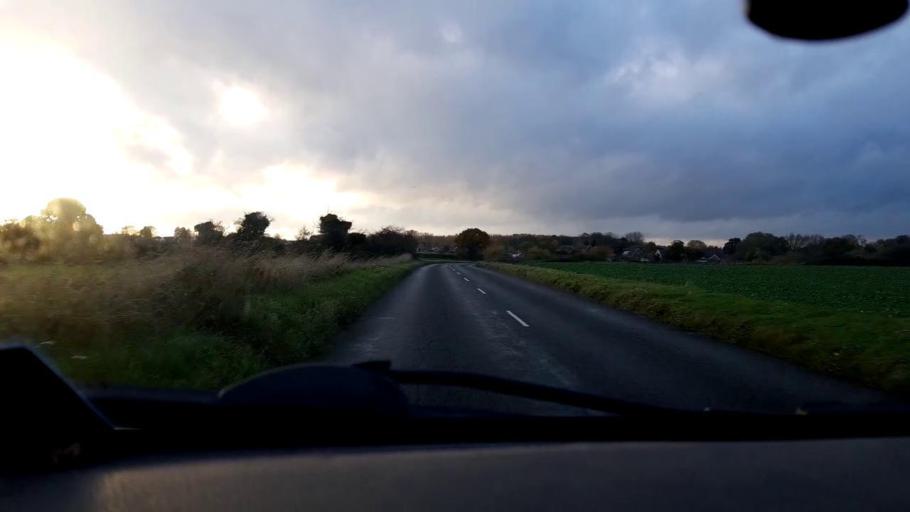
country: GB
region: England
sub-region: Norfolk
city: Spixworth
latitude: 52.6885
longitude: 1.2898
